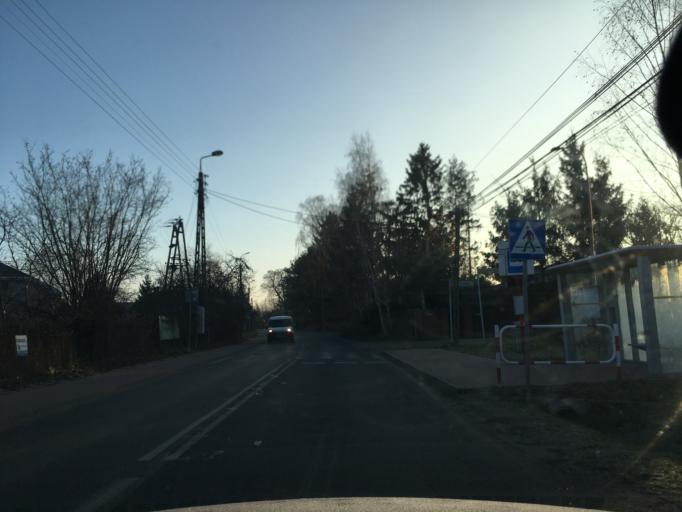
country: PL
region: Masovian Voivodeship
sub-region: Powiat piaseczynski
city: Piaseczno
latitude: 52.0696
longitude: 20.9858
